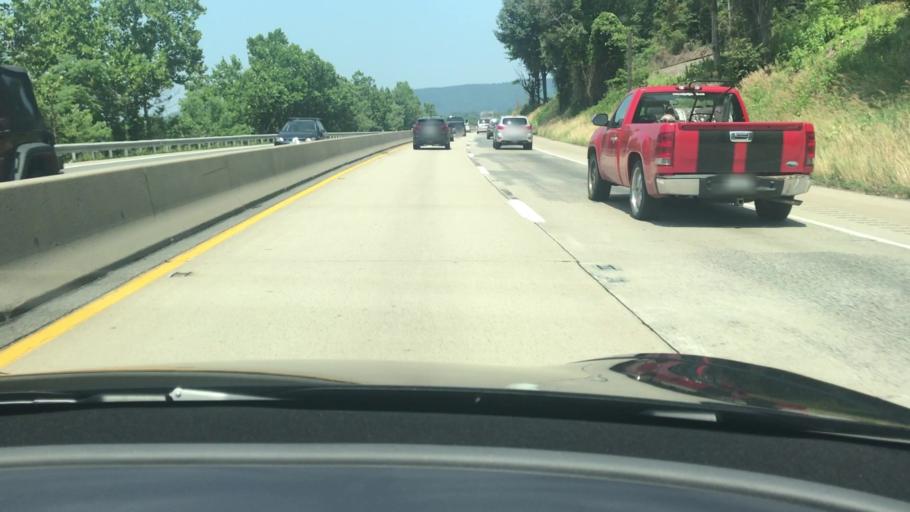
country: US
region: Pennsylvania
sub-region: Perry County
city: Marysville
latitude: 40.3542
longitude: -76.9199
